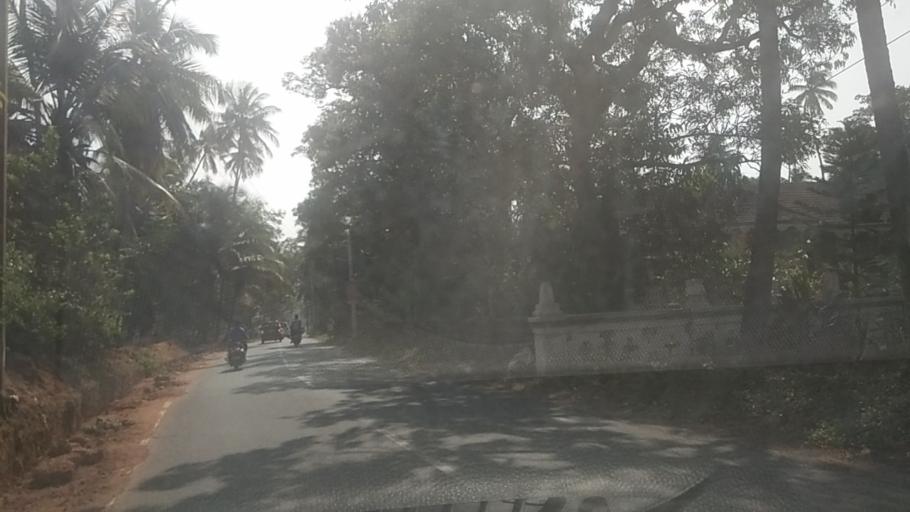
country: IN
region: Goa
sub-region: South Goa
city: Sancoale
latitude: 15.3363
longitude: 73.9010
